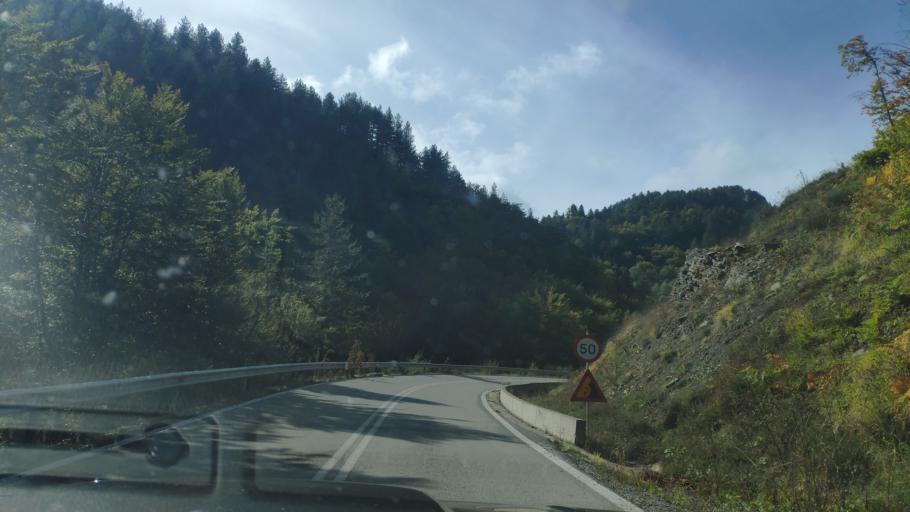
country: GR
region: West Macedonia
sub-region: Nomos Kastorias
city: Nestorio
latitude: 40.3735
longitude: 20.9376
